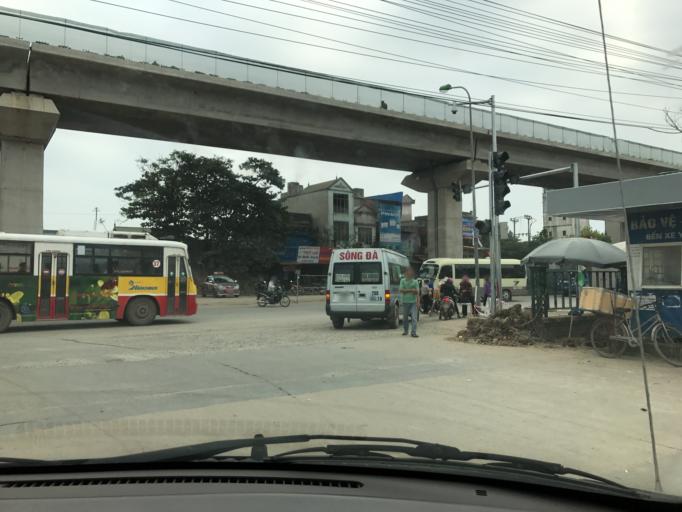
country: VN
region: Ha Noi
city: Ha Dong
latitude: 20.9491
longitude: 105.7469
